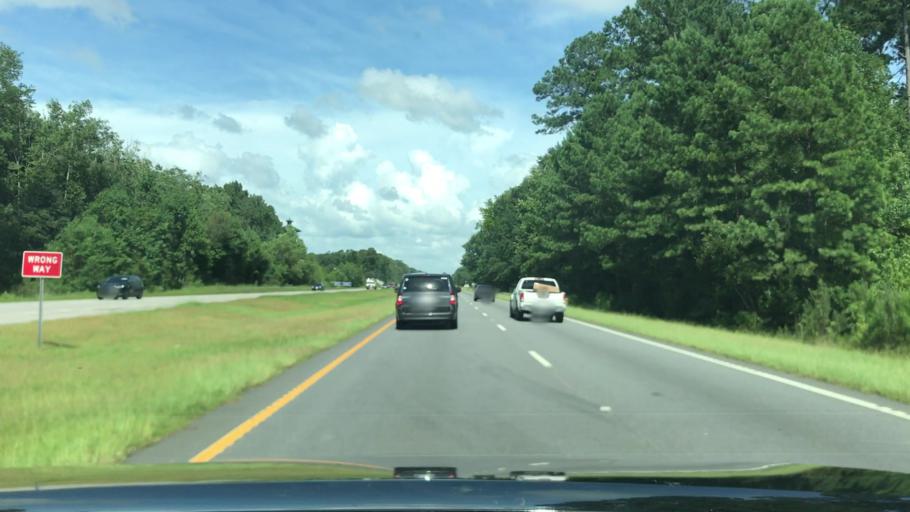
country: US
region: South Carolina
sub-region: Jasper County
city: Hardeeville
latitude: 32.3045
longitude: -81.0246
